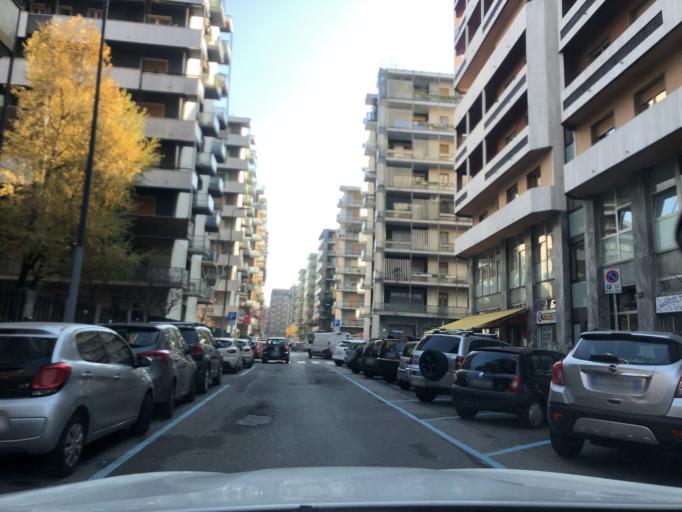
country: IT
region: Lombardy
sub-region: Citta metropolitana di Milano
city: Milano
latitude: 45.4965
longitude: 9.2038
